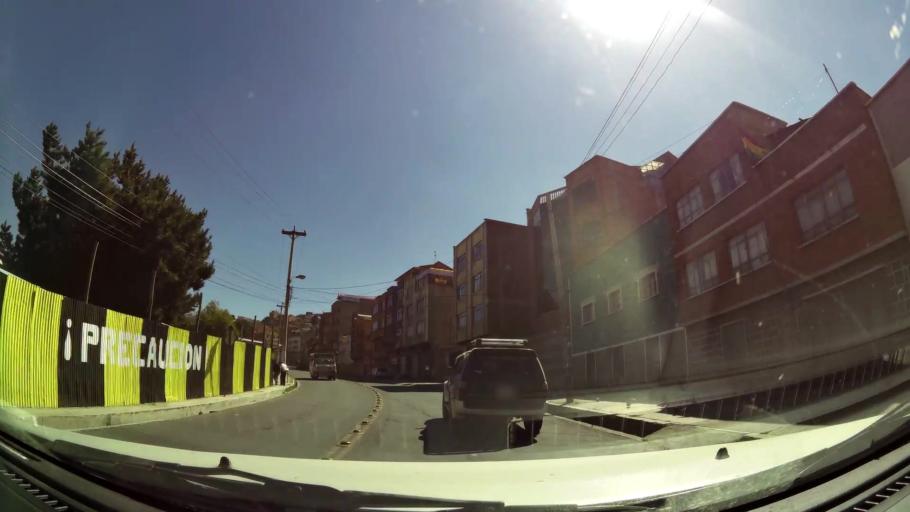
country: BO
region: La Paz
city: La Paz
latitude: -16.4869
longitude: -68.1558
